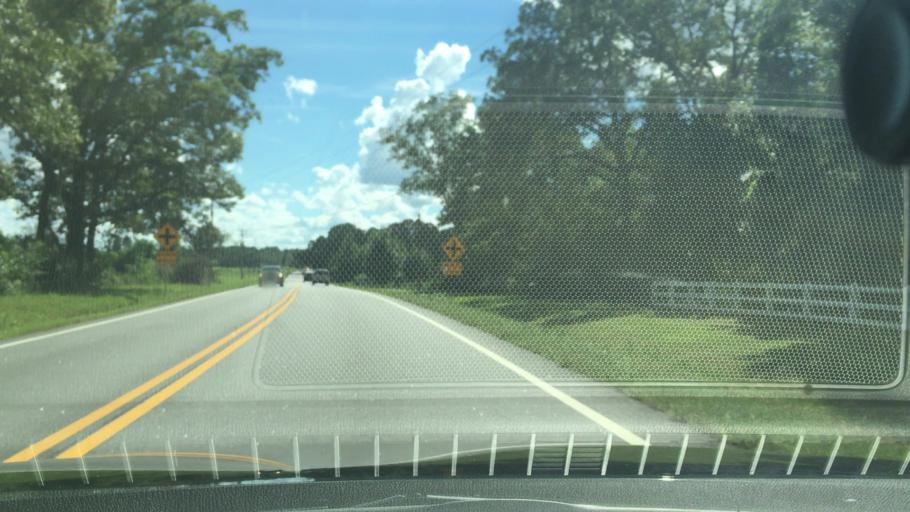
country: US
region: Georgia
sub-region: Butts County
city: Jackson
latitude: 33.2832
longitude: -84.0408
